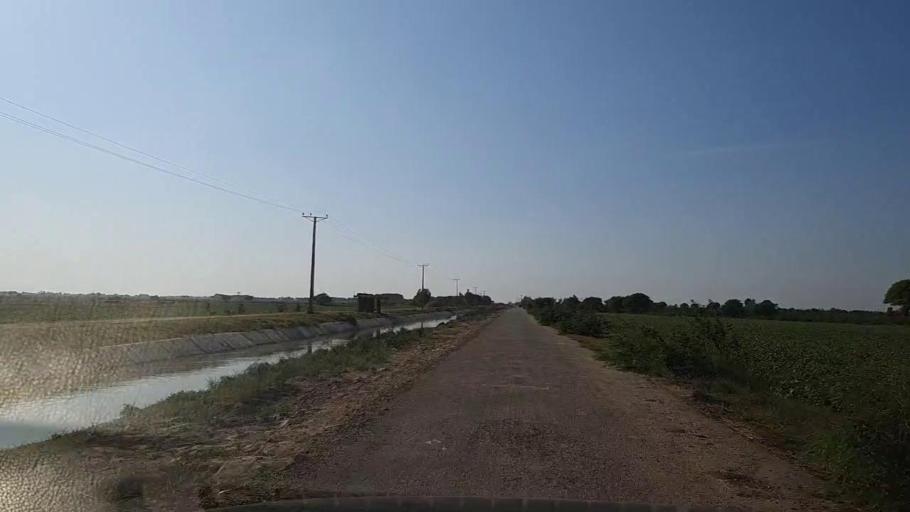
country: PK
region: Sindh
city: Mirpur Sakro
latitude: 24.5968
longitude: 67.8085
